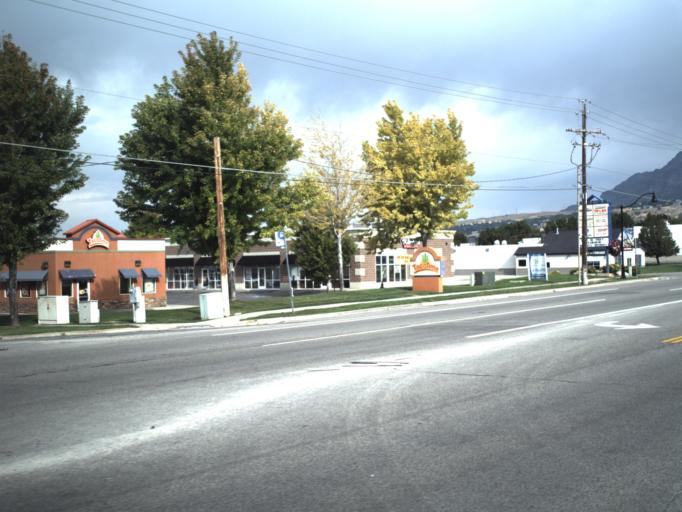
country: US
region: Utah
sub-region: Weber County
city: North Ogden
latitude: 41.3004
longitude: -111.9688
